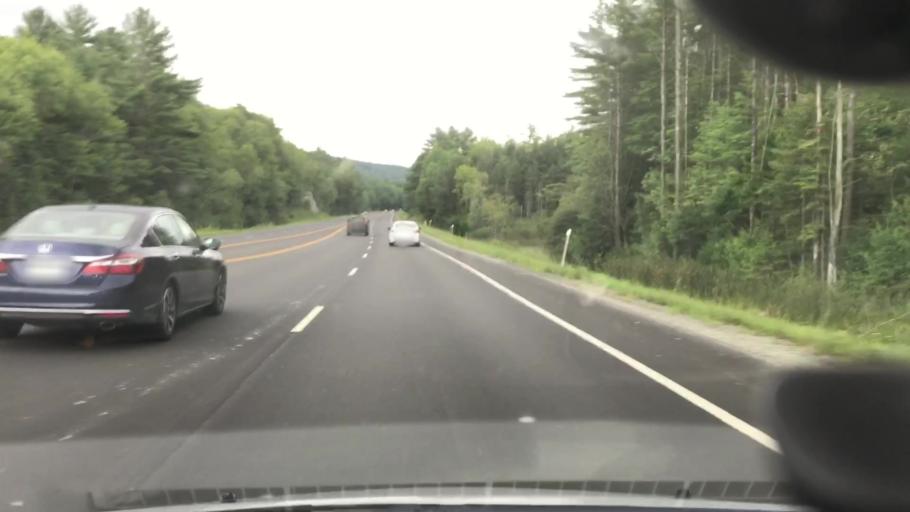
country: US
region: New Hampshire
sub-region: Grafton County
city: Lebanon
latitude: 43.6708
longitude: -72.2563
